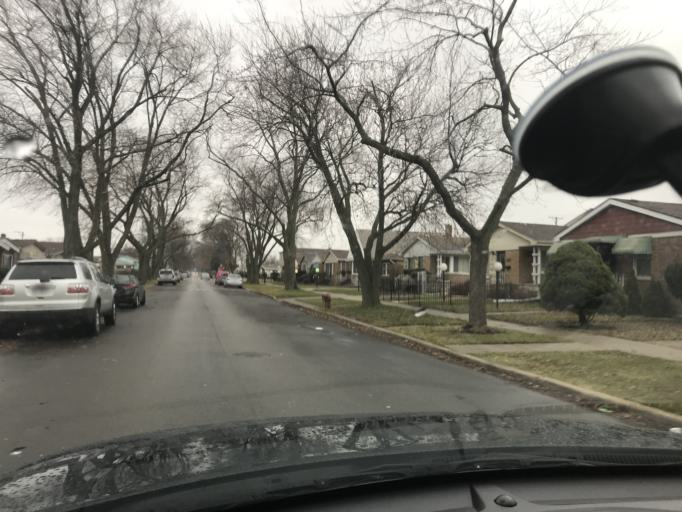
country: US
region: Illinois
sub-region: Cook County
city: Evergreen Park
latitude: 41.7265
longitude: -87.6373
